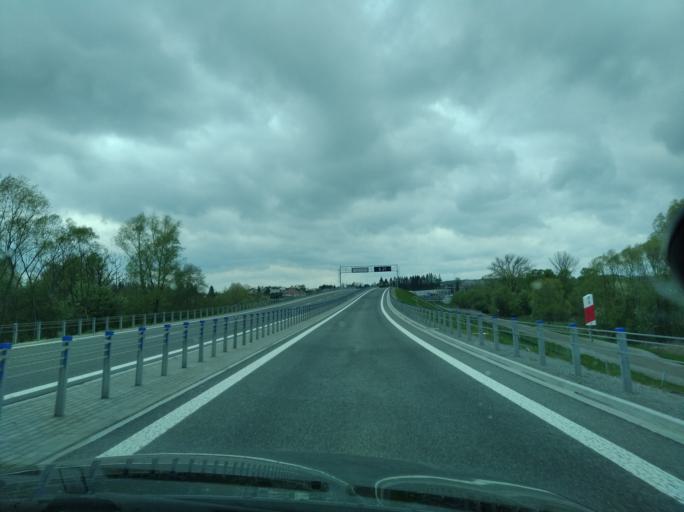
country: PL
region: Subcarpathian Voivodeship
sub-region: Powiat sanocki
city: Sanok
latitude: 49.5656
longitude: 22.1531
